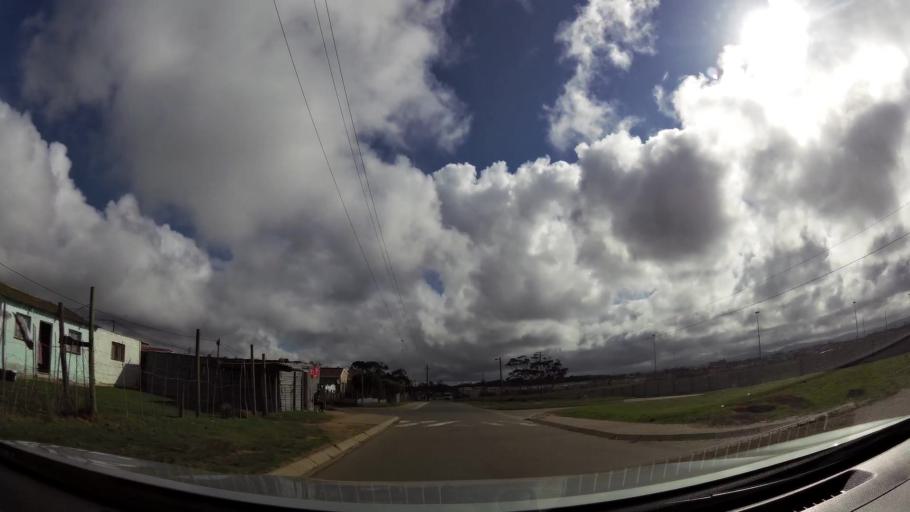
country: ZA
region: Western Cape
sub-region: Eden District Municipality
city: Plettenberg Bay
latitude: -34.0552
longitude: 23.3168
